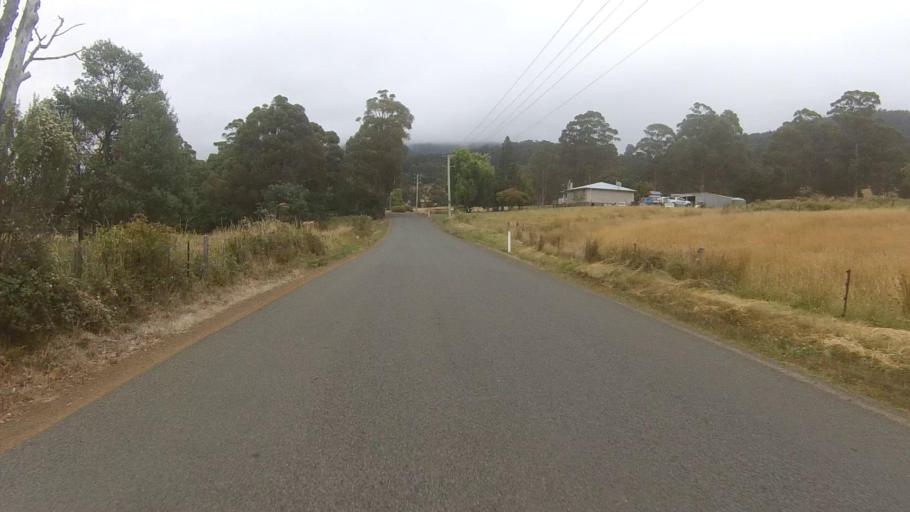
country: AU
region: Tasmania
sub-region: Kingborough
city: Margate
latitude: -42.9614
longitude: 147.2266
